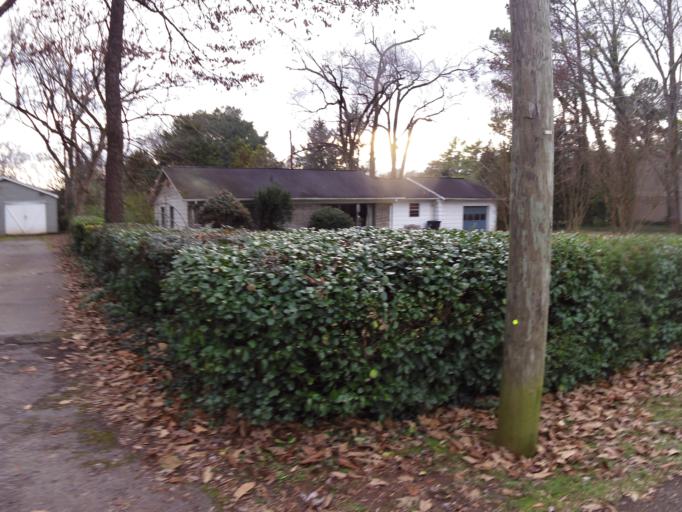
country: US
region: Tennessee
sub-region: Knox County
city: Knoxville
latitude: 35.9302
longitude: -83.9710
